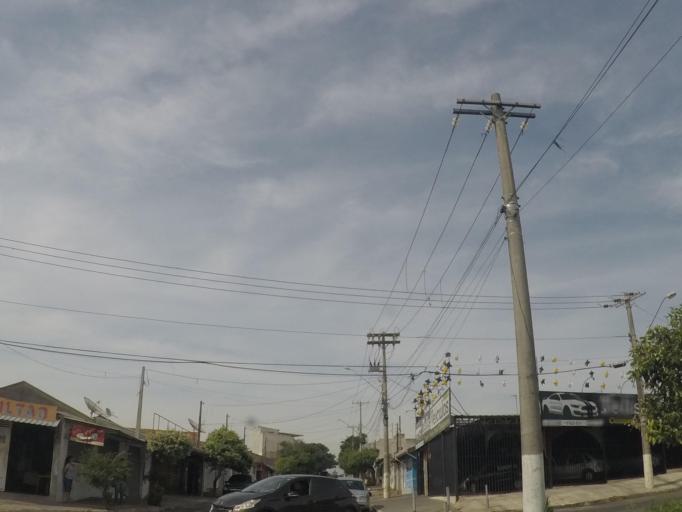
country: BR
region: Sao Paulo
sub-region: Hortolandia
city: Hortolandia
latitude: -22.8457
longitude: -47.1946
